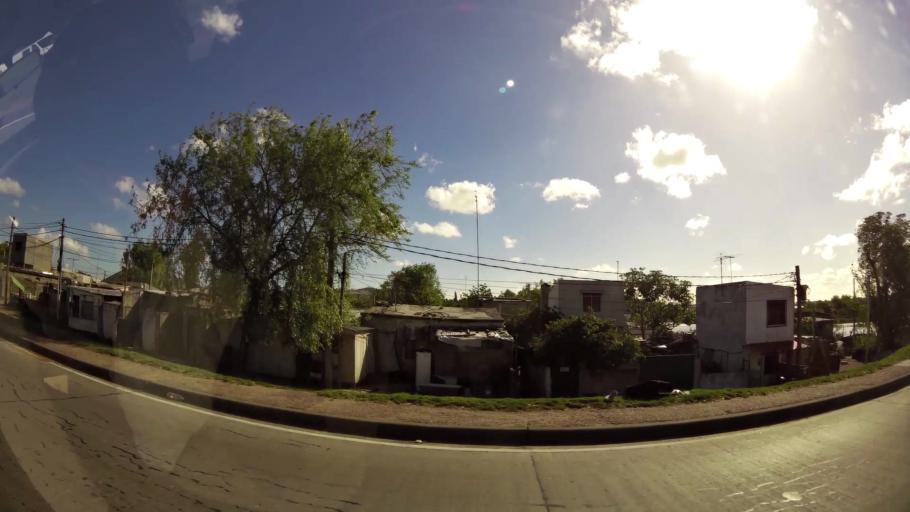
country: UY
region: Montevideo
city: Montevideo
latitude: -34.8692
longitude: -56.2438
